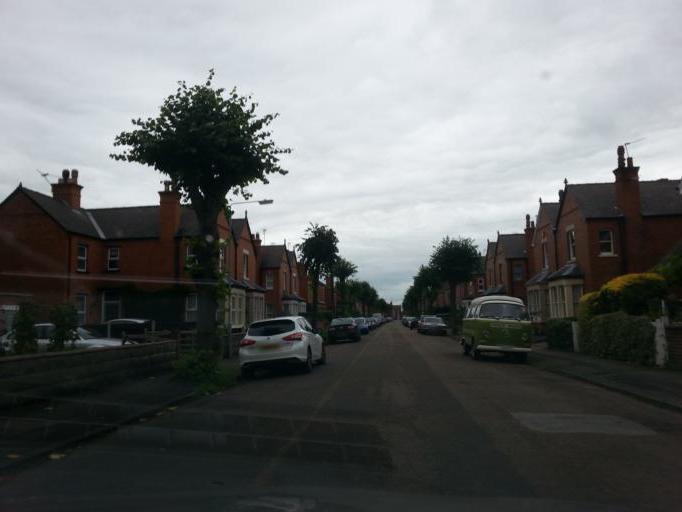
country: GB
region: England
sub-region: Nottinghamshire
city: Newark on Trent
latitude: 53.0702
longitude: -0.7988
